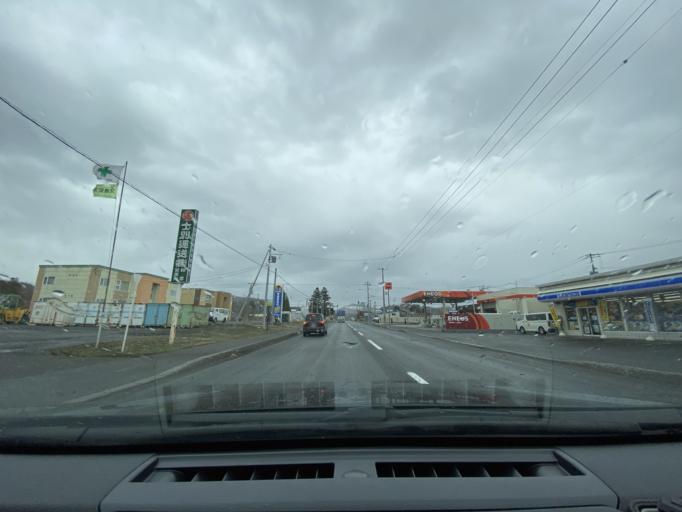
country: JP
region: Hokkaido
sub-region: Asahikawa-shi
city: Asahikawa
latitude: 44.0235
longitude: 142.4170
